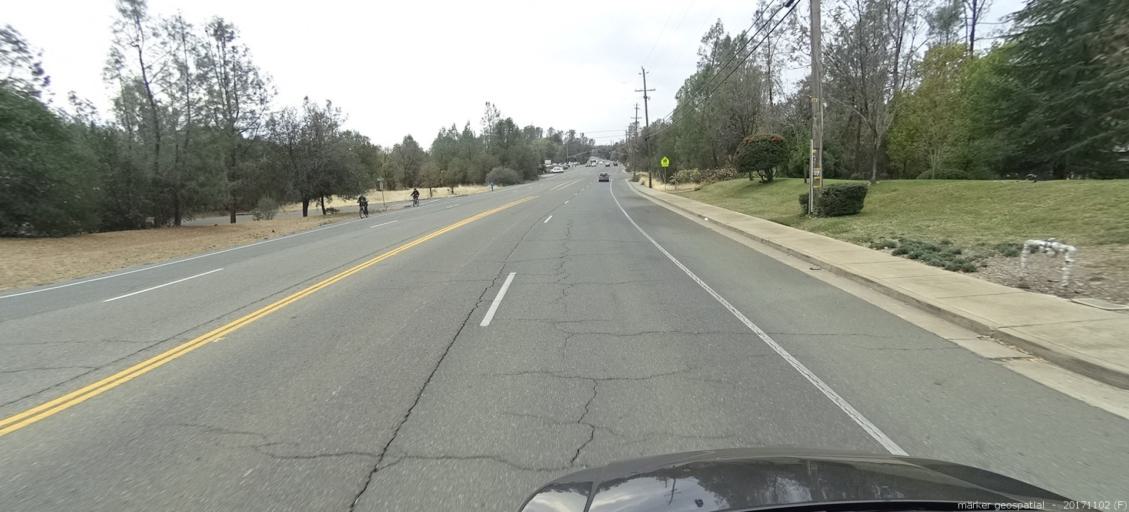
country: US
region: California
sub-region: Shasta County
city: Redding
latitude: 40.6334
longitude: -122.4049
